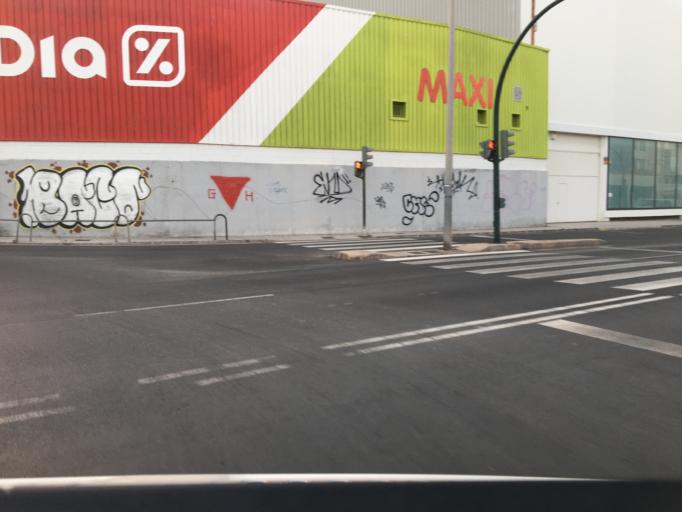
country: ES
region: Murcia
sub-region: Murcia
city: Cartagena
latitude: 37.6269
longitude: -1.0018
